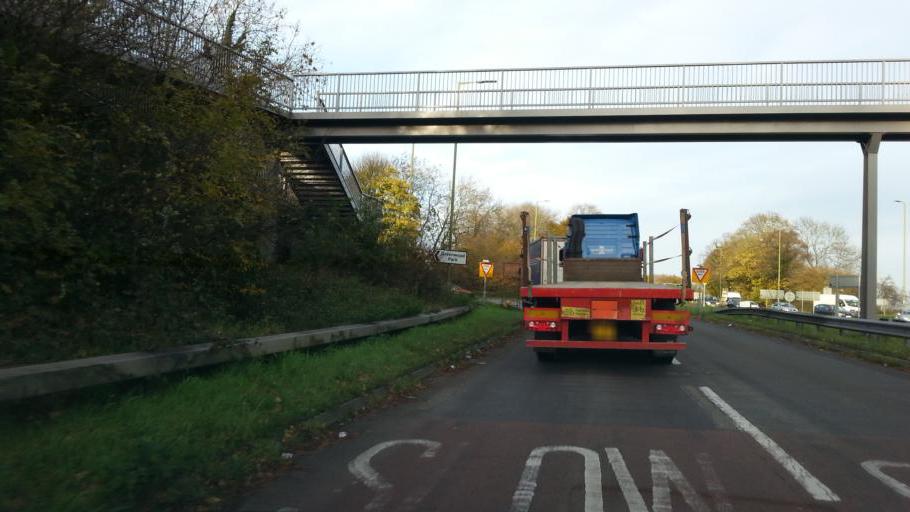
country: GB
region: England
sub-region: Hertfordshire
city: St Albans
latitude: 51.7255
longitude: -0.3543
